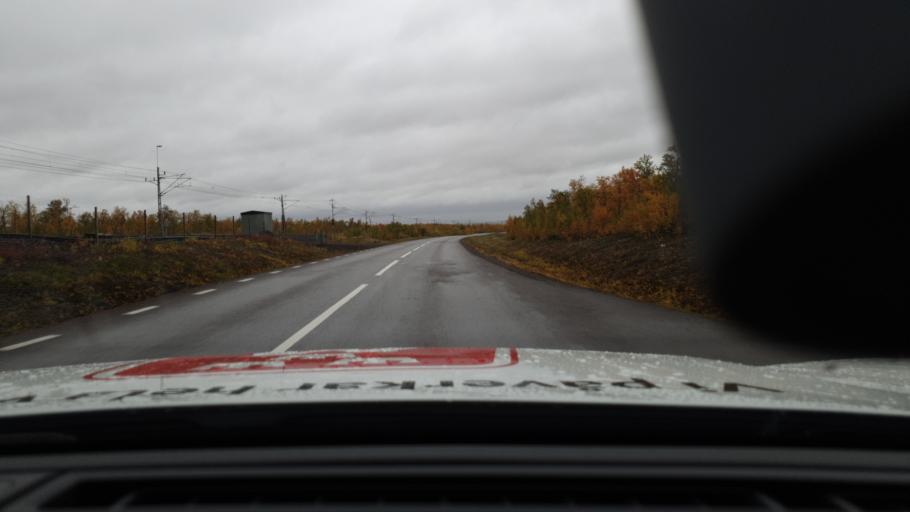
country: SE
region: Norrbotten
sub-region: Kiruna Kommun
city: Kiruna
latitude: 67.8843
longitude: 20.1407
